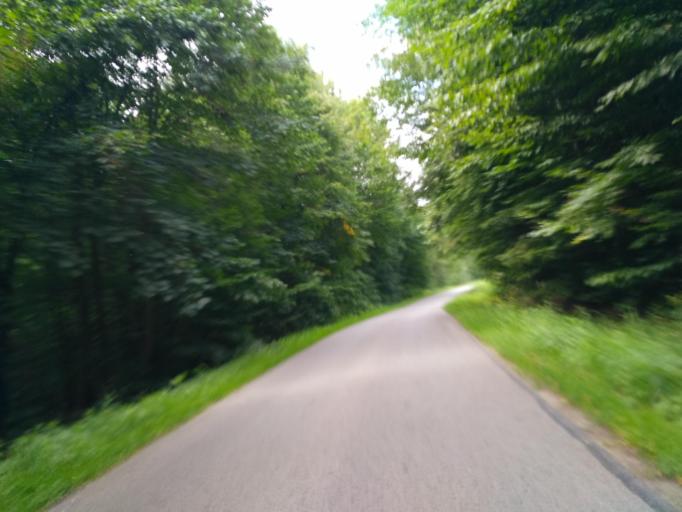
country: PL
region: Subcarpathian Voivodeship
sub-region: Powiat rzeszowski
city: Chmielnik
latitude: 49.9517
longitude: 22.1348
